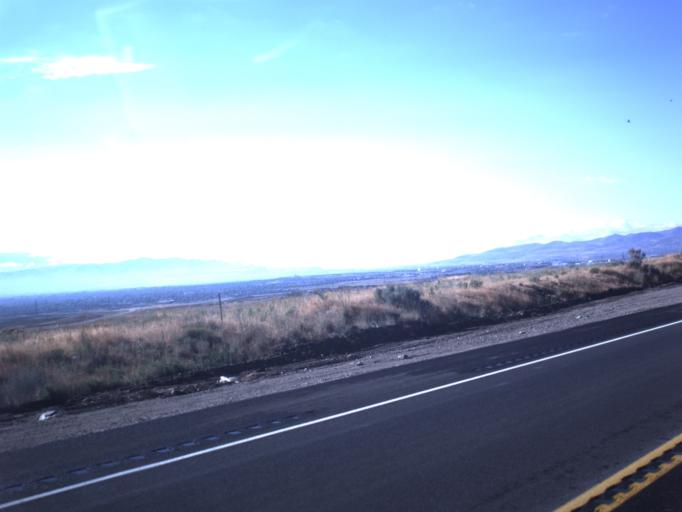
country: US
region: Utah
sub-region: Salt Lake County
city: Oquirrh
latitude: 40.6251
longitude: -112.0527
